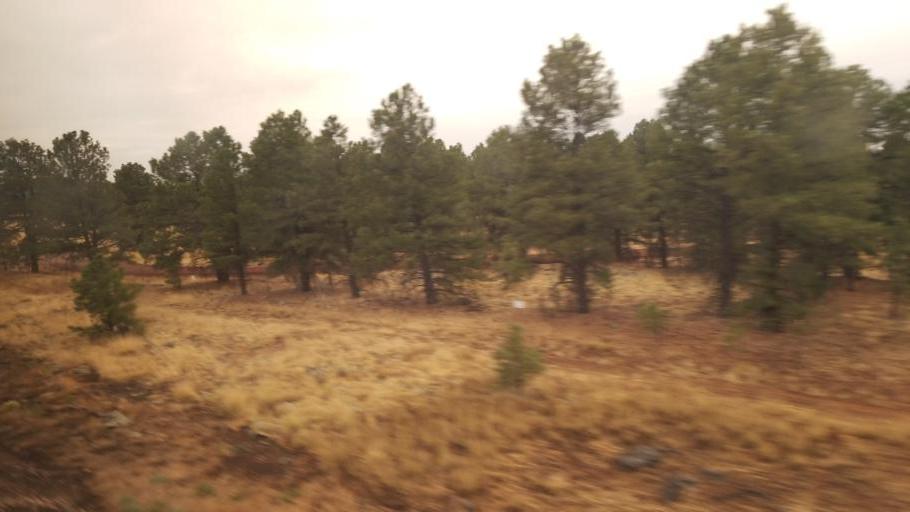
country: US
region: Arizona
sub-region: Coconino County
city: Parks
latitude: 35.2275
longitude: -111.8093
